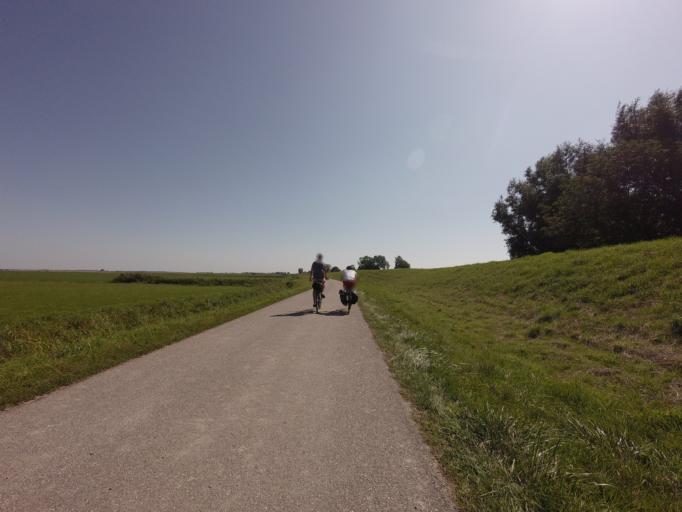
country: NL
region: Friesland
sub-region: Gemeente Dongeradeel
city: Anjum
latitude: 53.3942
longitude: 6.1121
